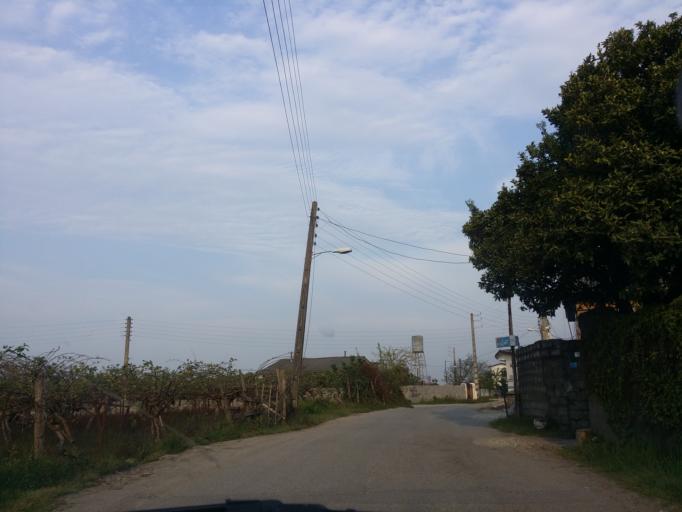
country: IR
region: Mazandaran
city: Chalus
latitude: 36.6657
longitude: 51.3720
